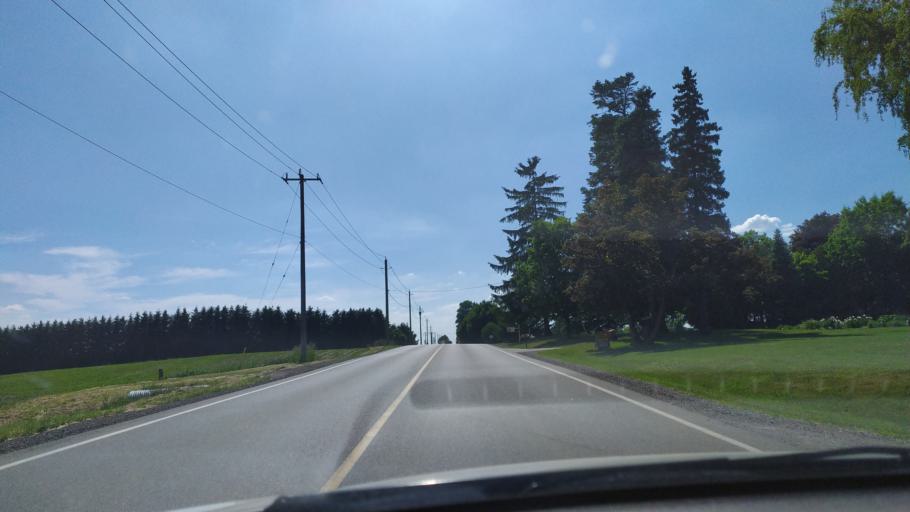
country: CA
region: Ontario
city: Kitchener
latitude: 43.3783
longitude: -80.5115
